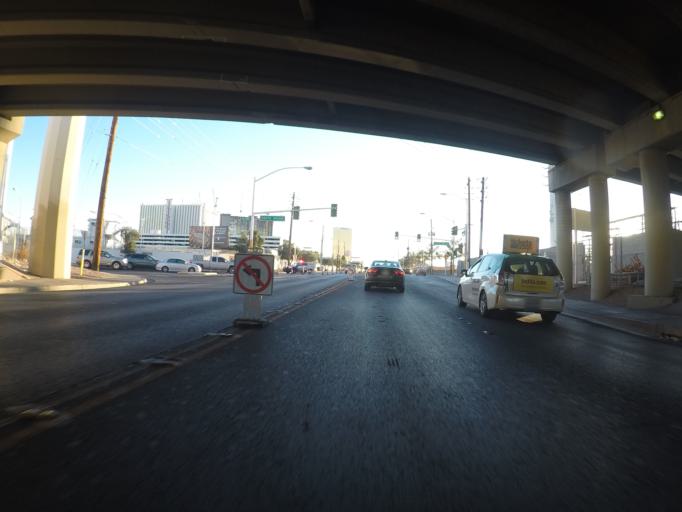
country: US
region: Nevada
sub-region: Clark County
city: Las Vegas
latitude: 36.1439
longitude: -115.1649
